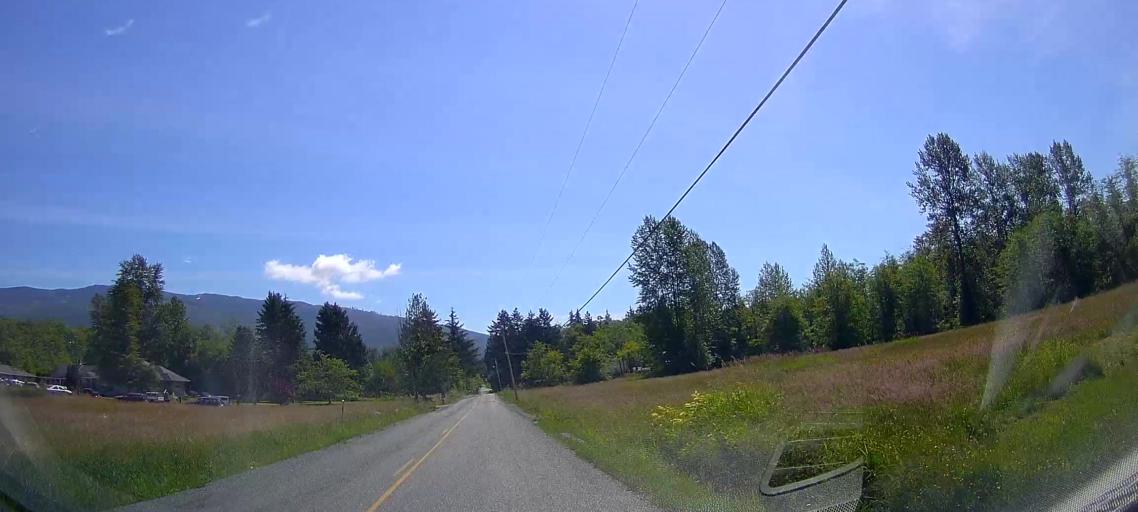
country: US
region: Washington
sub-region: Skagit County
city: Sedro-Woolley
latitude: 48.5579
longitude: -122.2536
